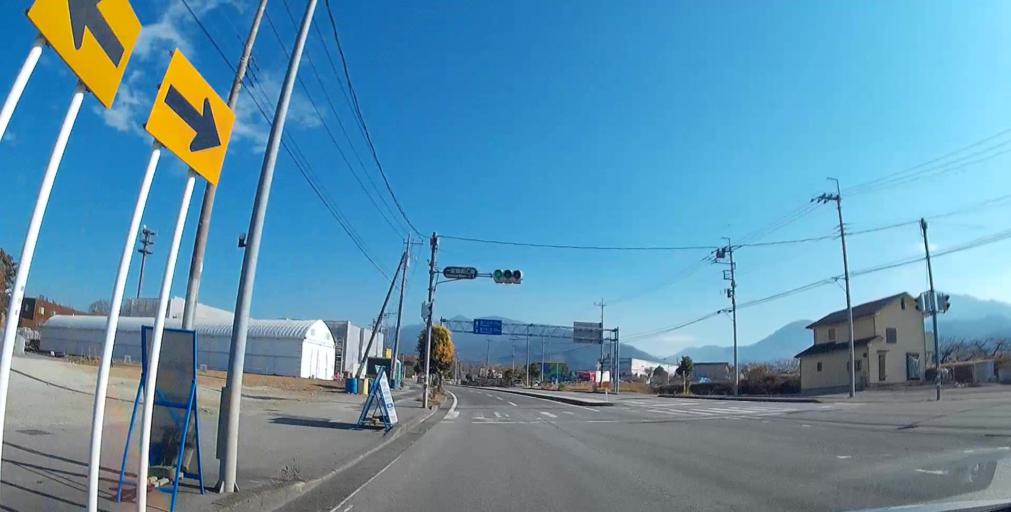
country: JP
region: Yamanashi
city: Isawa
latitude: 35.6327
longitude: 138.6762
